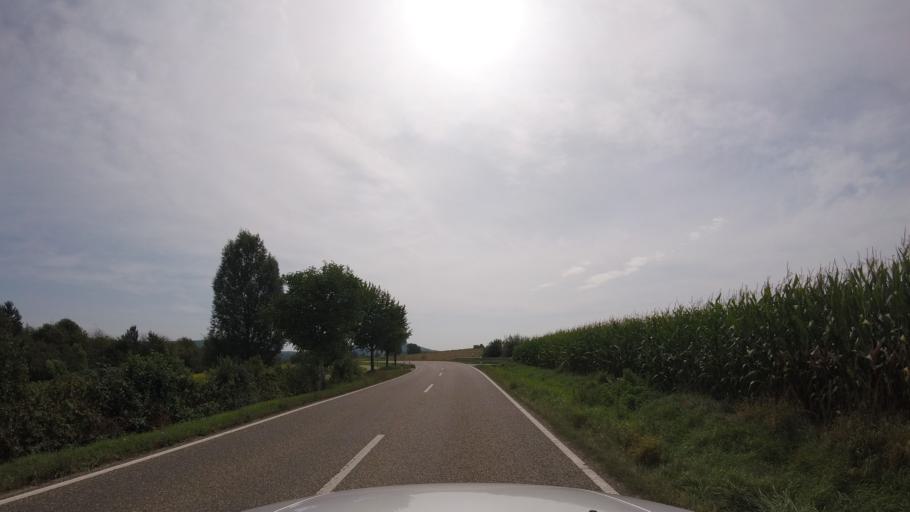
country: DE
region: Baden-Wuerttemberg
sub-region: Regierungsbezirk Stuttgart
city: Grossbottwar
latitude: 49.0092
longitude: 9.2778
